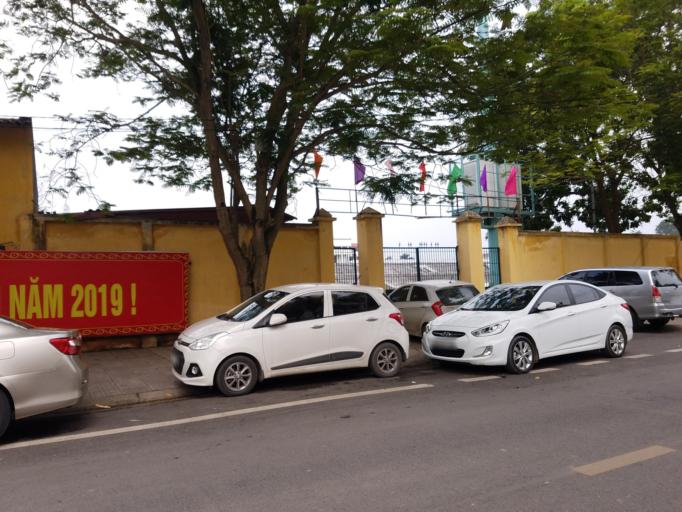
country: VN
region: Thai Nguyen
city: Thanh Pho Thai Nguyen
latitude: 21.5947
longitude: 105.8421
